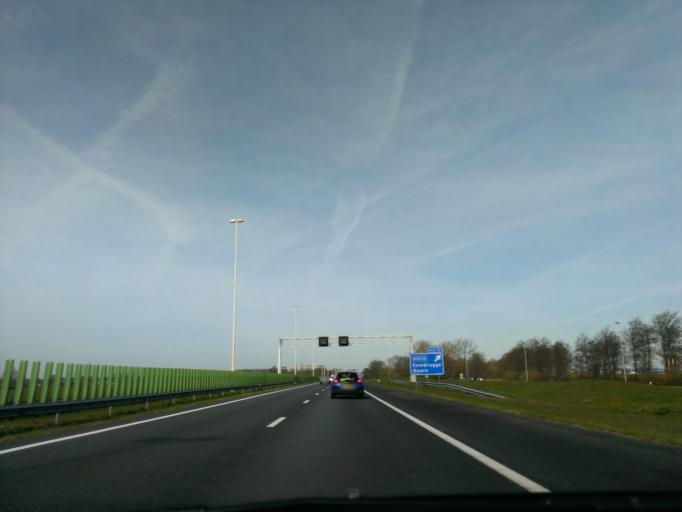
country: NL
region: Utrecht
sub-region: Gemeente Baarn
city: Baarn
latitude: 52.2160
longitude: 5.3219
